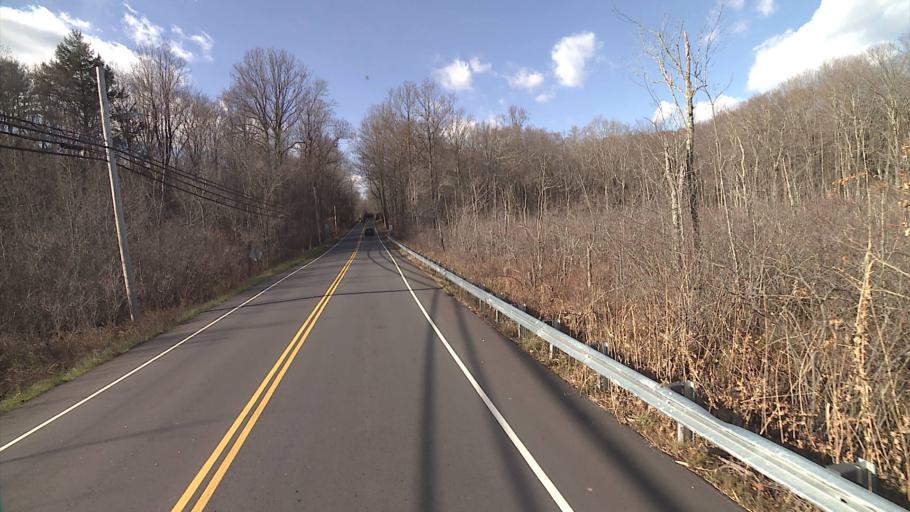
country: US
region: Connecticut
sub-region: Fairfield County
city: Georgetown
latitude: 41.3068
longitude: -73.4052
